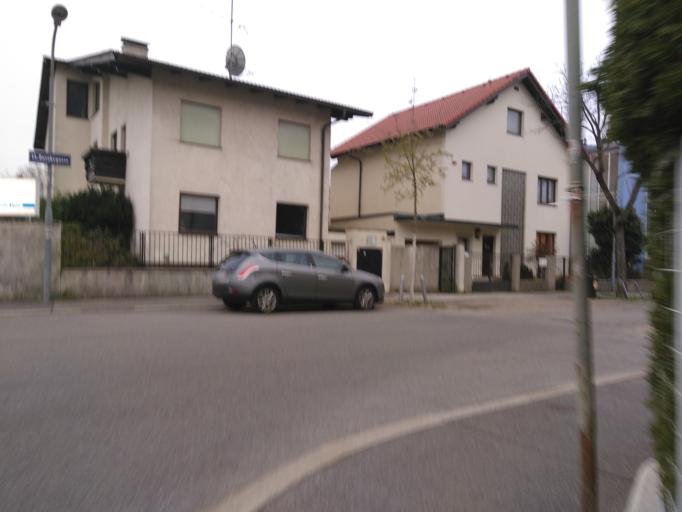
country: AT
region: Lower Austria
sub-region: Politischer Bezirk Modling
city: Perchtoldsdorf
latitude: 48.1751
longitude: 16.2921
